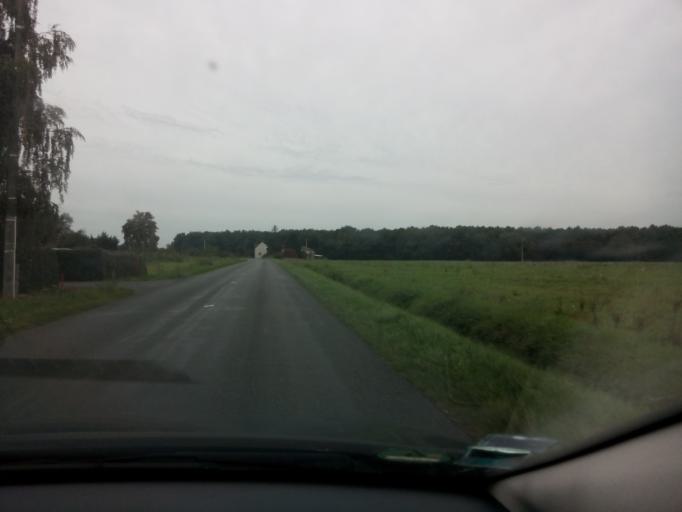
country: FR
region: Pays de la Loire
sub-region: Departement de Maine-et-Loire
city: Baune
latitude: 47.4971
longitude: -0.3296
